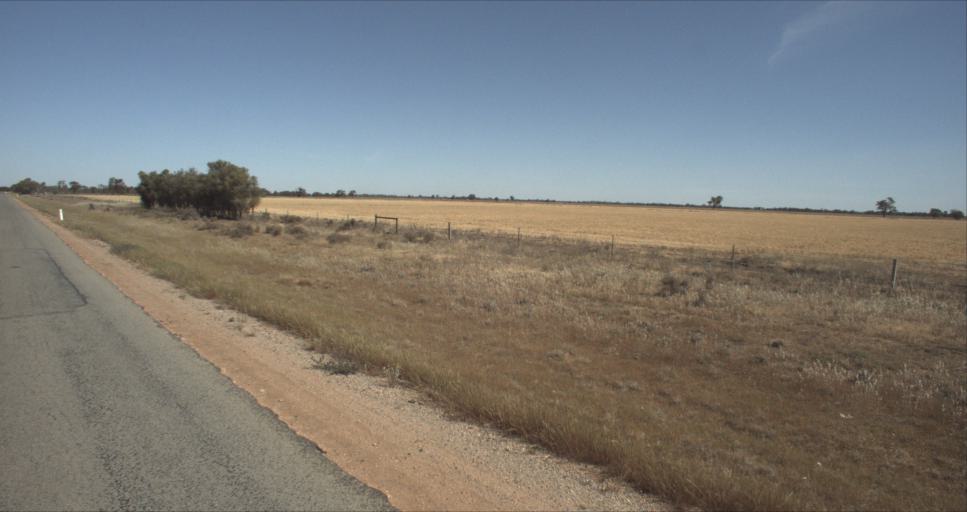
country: AU
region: New South Wales
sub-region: Leeton
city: Leeton
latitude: -34.4942
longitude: 146.3871
